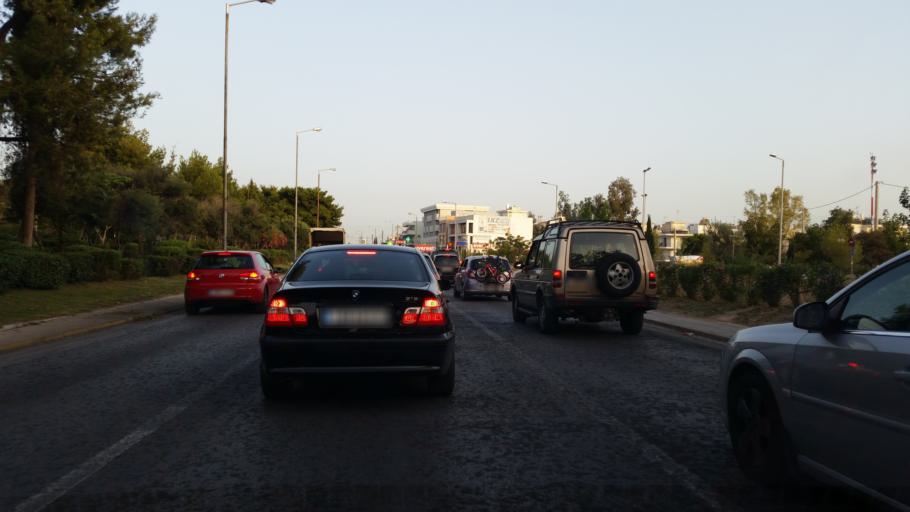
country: GR
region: Attica
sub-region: Nomarchia Athinas
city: Elliniko
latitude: 37.8890
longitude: 23.7490
